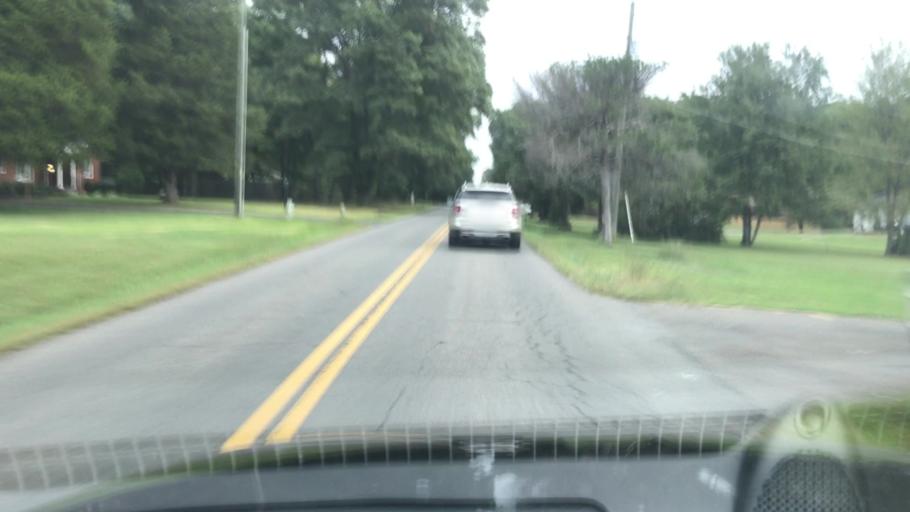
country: US
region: Virginia
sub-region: Fauquier County
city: New Baltimore
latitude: 38.7135
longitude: -77.6640
